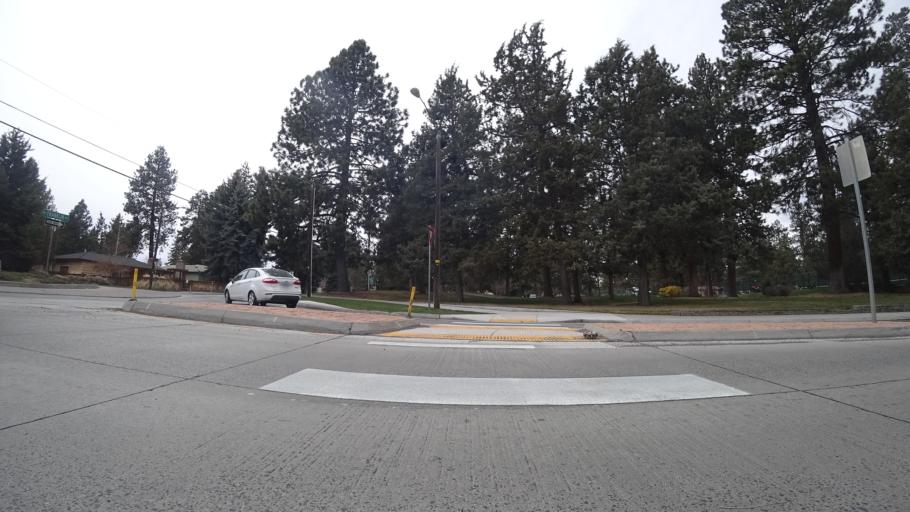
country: US
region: Oregon
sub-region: Deschutes County
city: Bend
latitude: 44.0562
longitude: -121.2938
